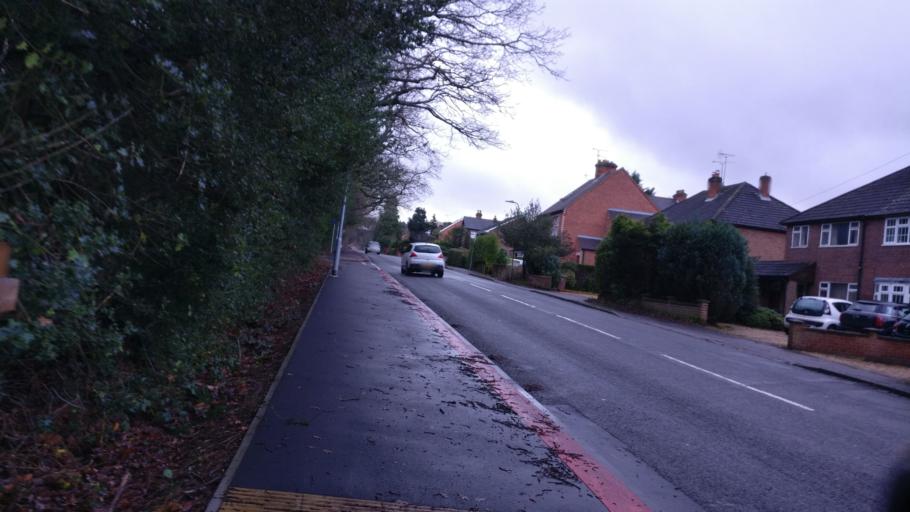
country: GB
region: England
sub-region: Bracknell Forest
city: Crowthorne
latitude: 51.3757
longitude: -0.7900
